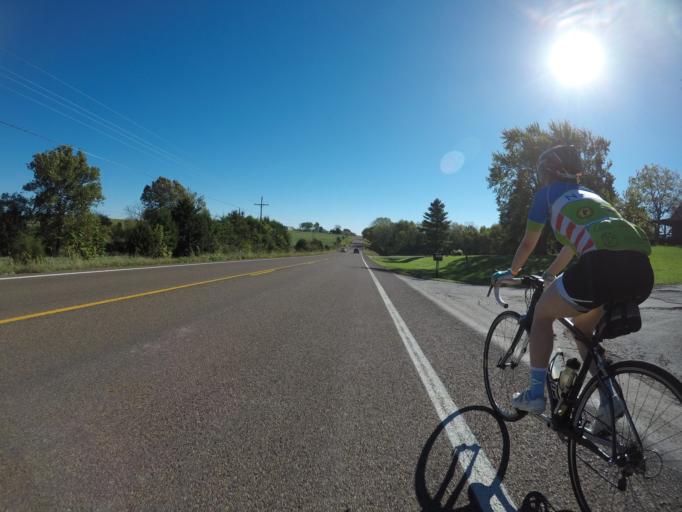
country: US
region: Kansas
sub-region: Wyandotte County
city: Bonner Springs
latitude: 39.0581
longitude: -94.9616
